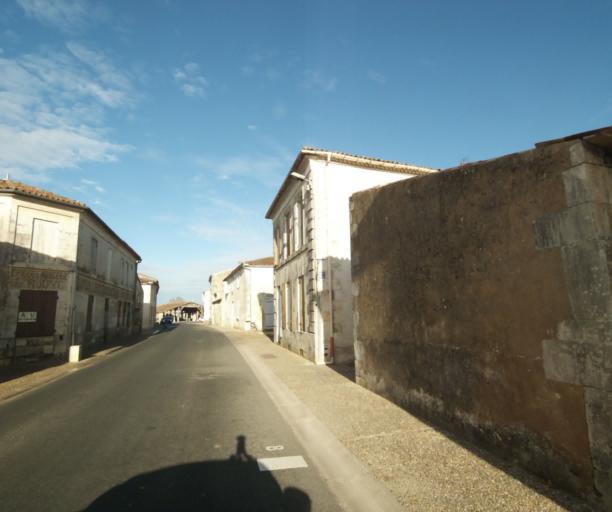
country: FR
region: Poitou-Charentes
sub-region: Departement de la Charente-Maritime
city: Corme-Royal
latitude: 45.7008
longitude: -0.7809
